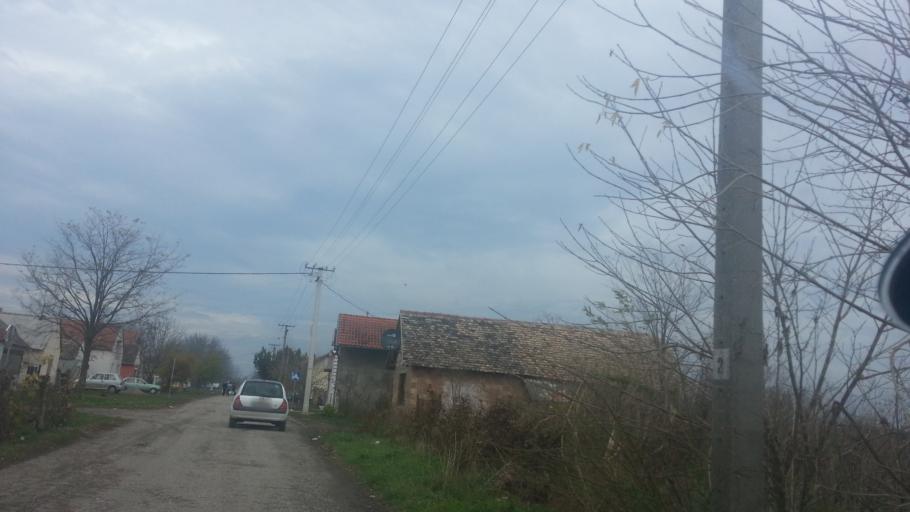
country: RS
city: Golubinci
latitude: 44.9817
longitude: 20.0806
